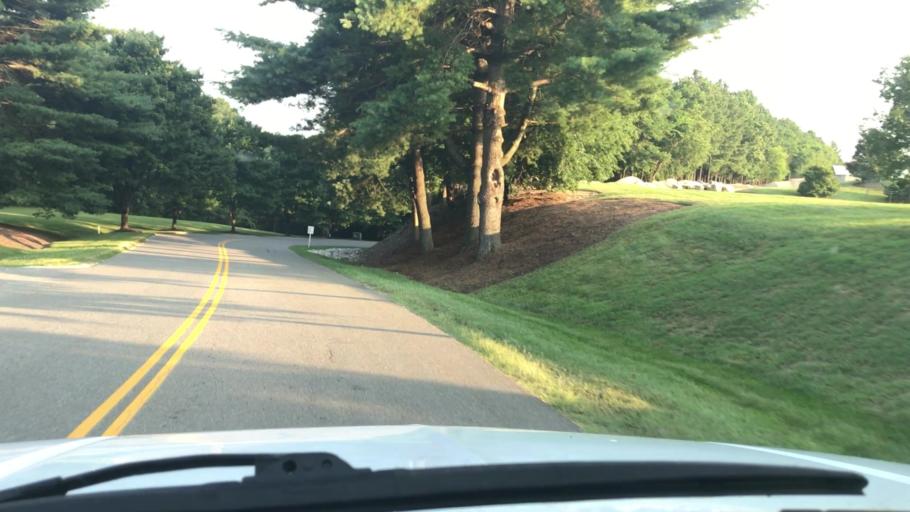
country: US
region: Virginia
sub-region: Henrico County
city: Short Pump
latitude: 37.6007
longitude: -77.7120
